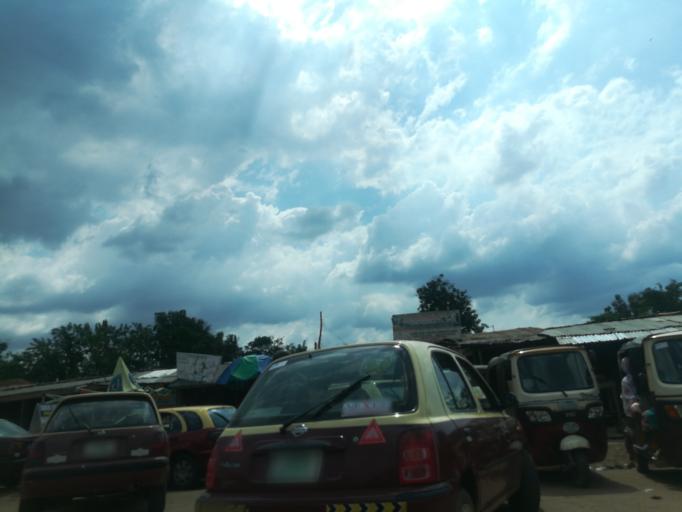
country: NG
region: Oyo
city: Ibadan
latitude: 7.4197
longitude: 3.8591
